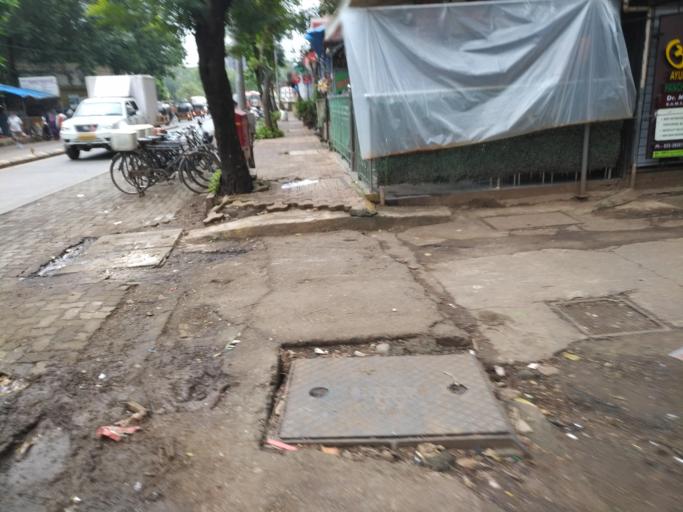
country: IN
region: Maharashtra
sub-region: Mumbai Suburban
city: Borivli
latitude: 19.2341
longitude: 72.8641
